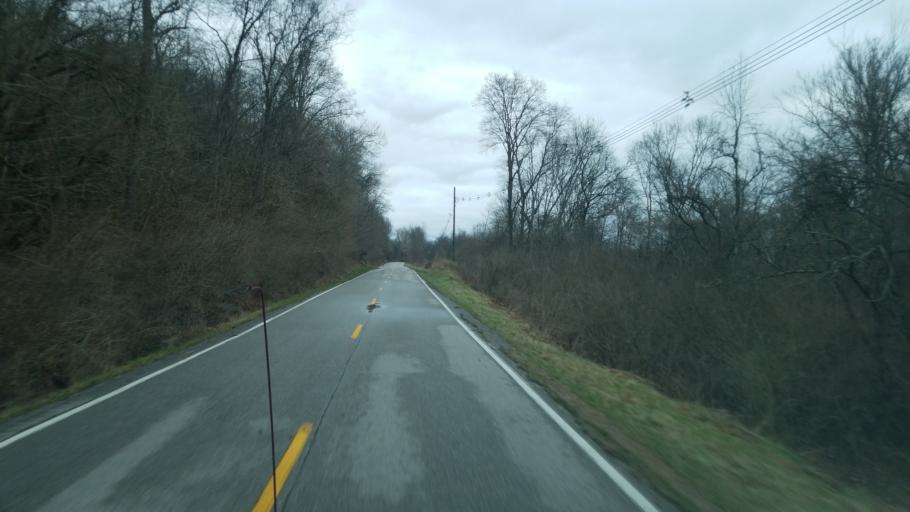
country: US
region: Ohio
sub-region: Clermont County
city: New Richmond
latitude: 38.9003
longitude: -84.2559
